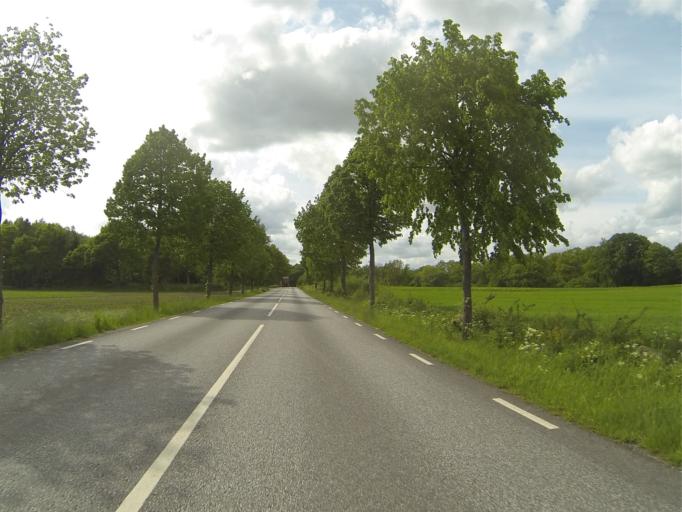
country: SE
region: Skane
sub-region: Sjobo Kommun
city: Sjoebo
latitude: 55.6812
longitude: 13.6437
